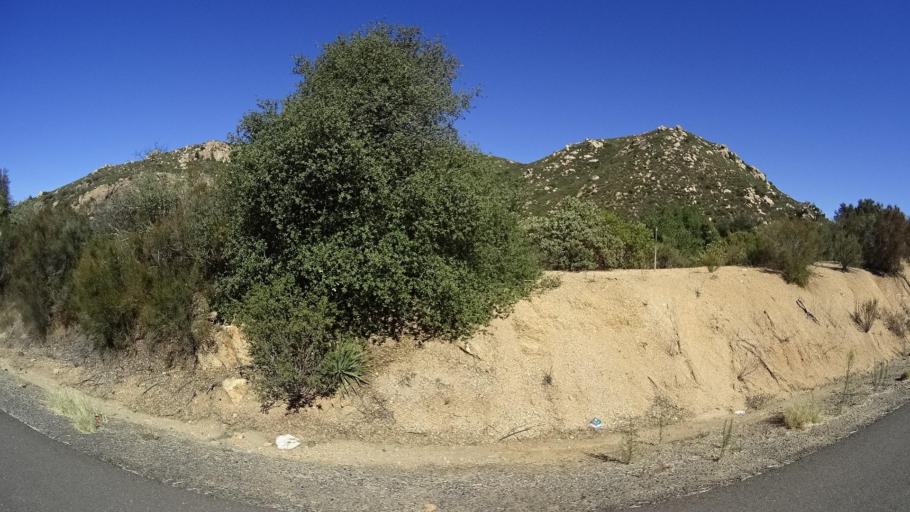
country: US
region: California
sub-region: San Diego County
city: Descanso
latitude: 32.8368
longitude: -116.6177
